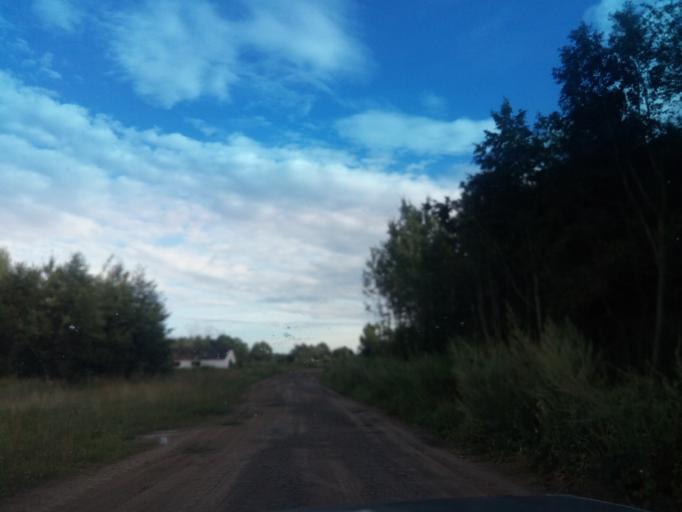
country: BY
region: Vitebsk
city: Dzisna
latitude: 55.6753
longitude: 28.3489
